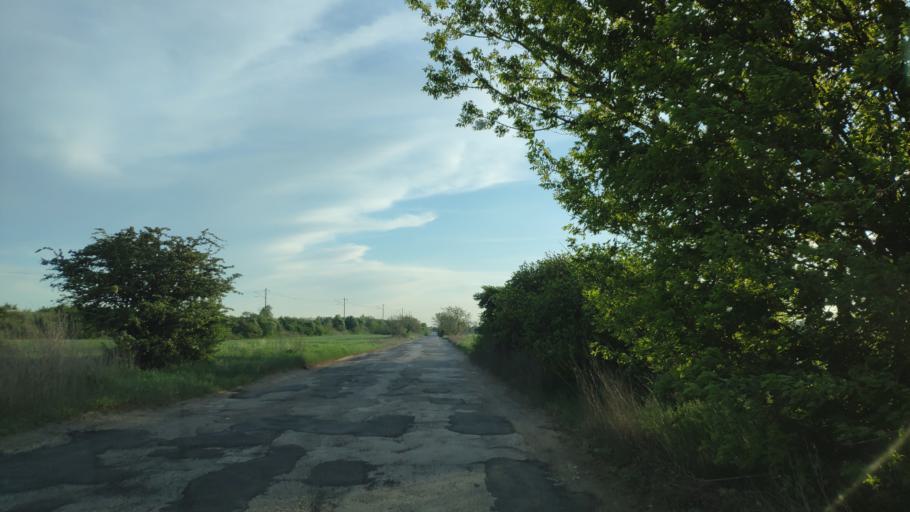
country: SK
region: Kosicky
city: Kosice
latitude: 48.6512
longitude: 21.3014
